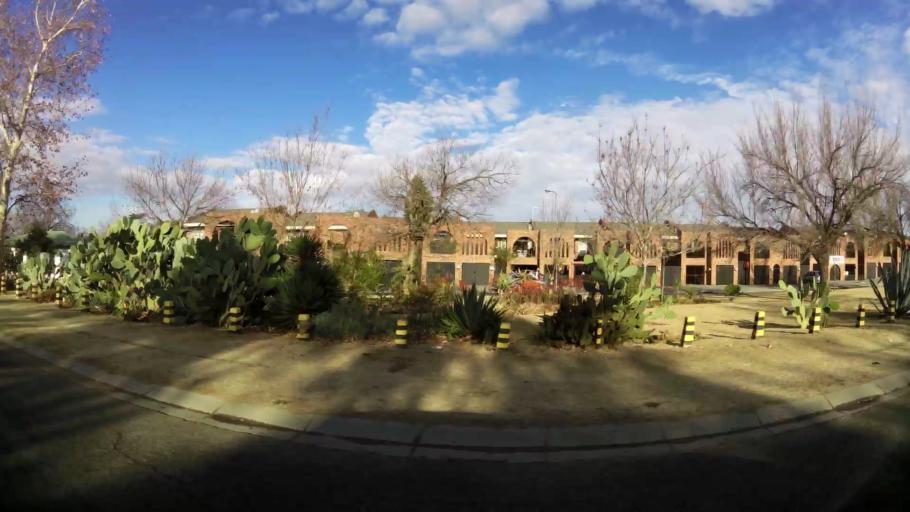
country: ZA
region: Orange Free State
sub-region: Lejweleputswa District Municipality
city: Welkom
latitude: -27.9899
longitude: 26.7526
